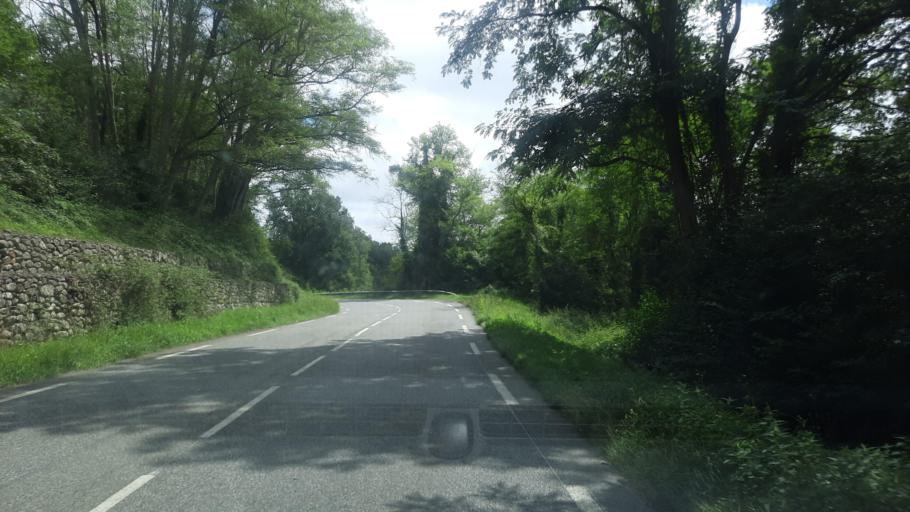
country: FR
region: Midi-Pyrenees
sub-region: Departement des Hautes-Pyrenees
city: Trie-sur-Baise
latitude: 43.2991
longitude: 0.2780
